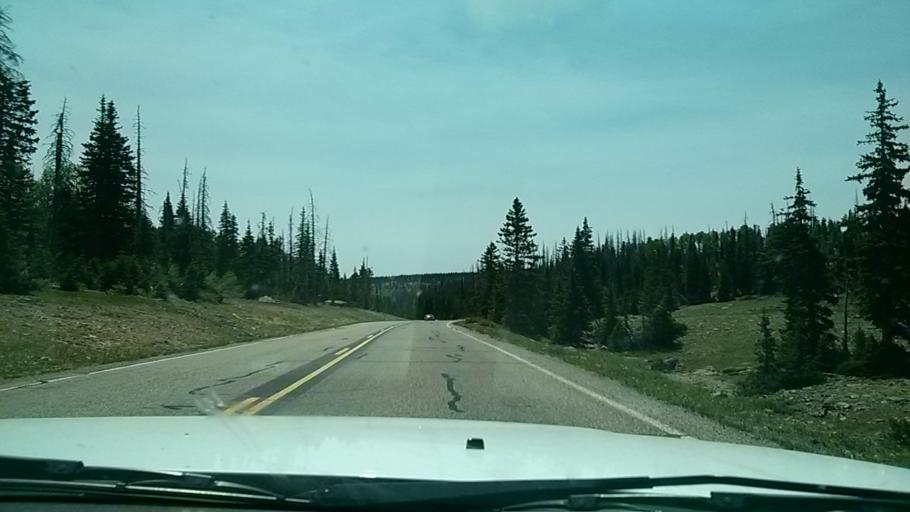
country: US
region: Utah
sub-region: Iron County
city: Cedar City
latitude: 37.5870
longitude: -112.8478
